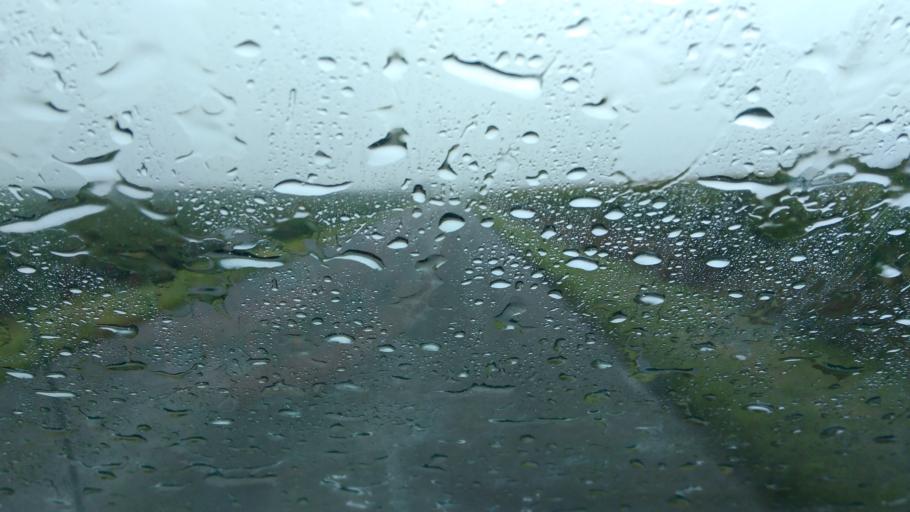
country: US
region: Ohio
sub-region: Hardin County
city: Kenton
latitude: 40.6922
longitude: -83.5379
